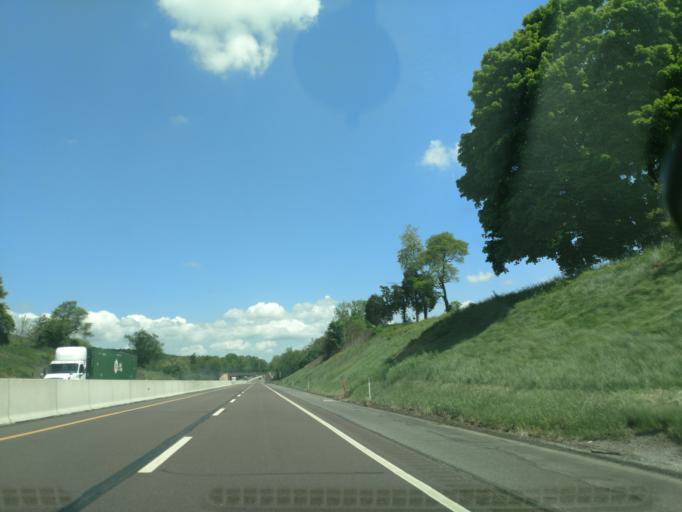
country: US
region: Pennsylvania
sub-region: Lancaster County
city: Clay
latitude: 40.2402
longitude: -76.2538
